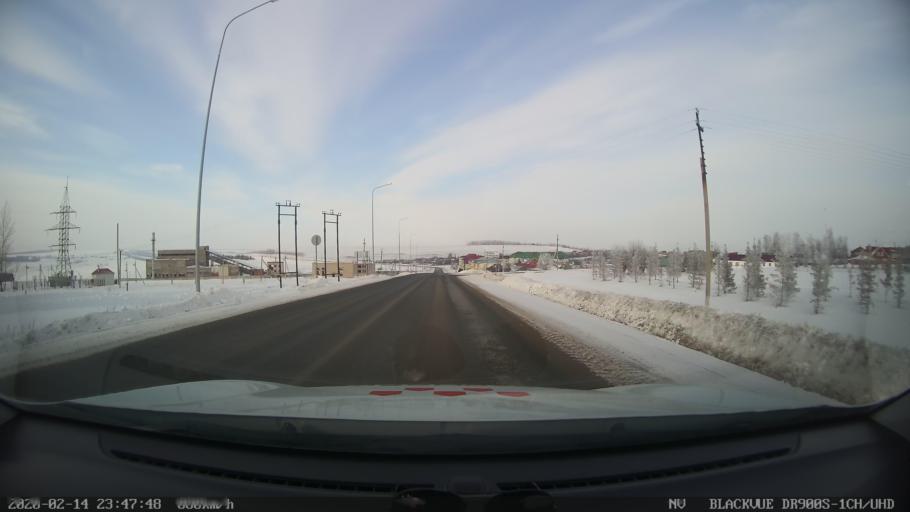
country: RU
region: Tatarstan
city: Kuybyshevskiy Zaton
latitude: 55.2429
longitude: 49.2068
